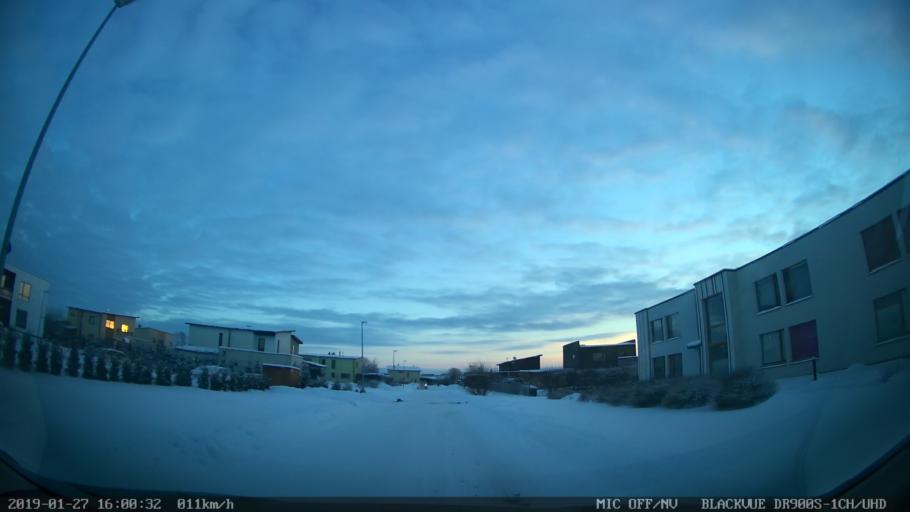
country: EE
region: Harju
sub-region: Tallinna linn
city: Tallinn
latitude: 59.3984
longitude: 24.8004
